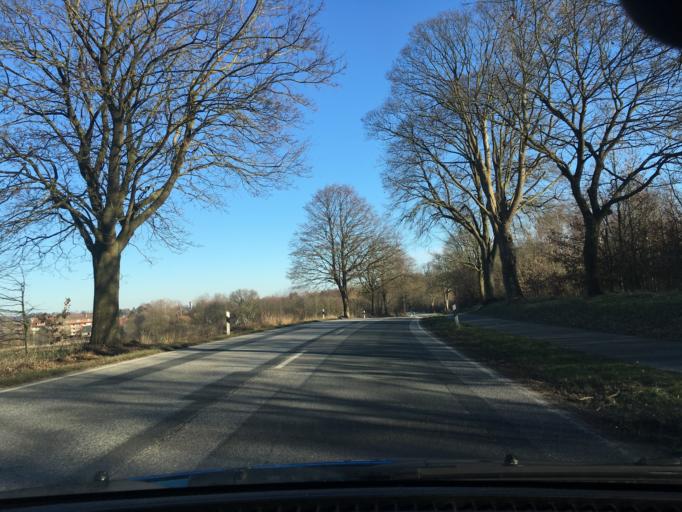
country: DE
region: Schleswig-Holstein
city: Schnakenbek
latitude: 53.3745
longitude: 10.5248
